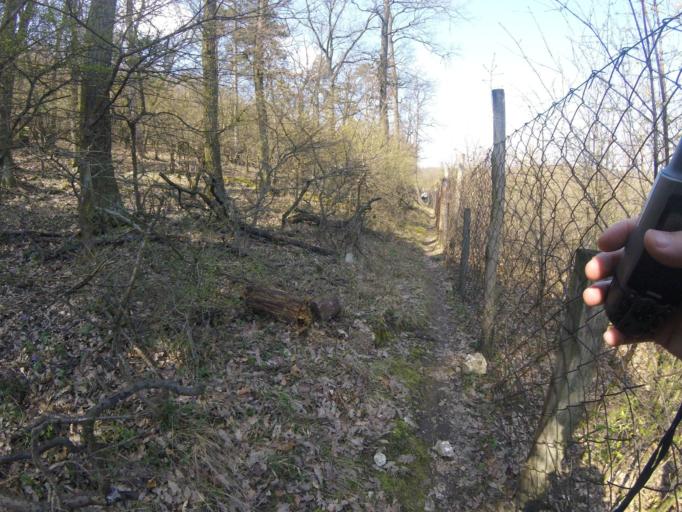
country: HU
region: Pest
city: Budakeszi
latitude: 47.5371
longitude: 18.9276
